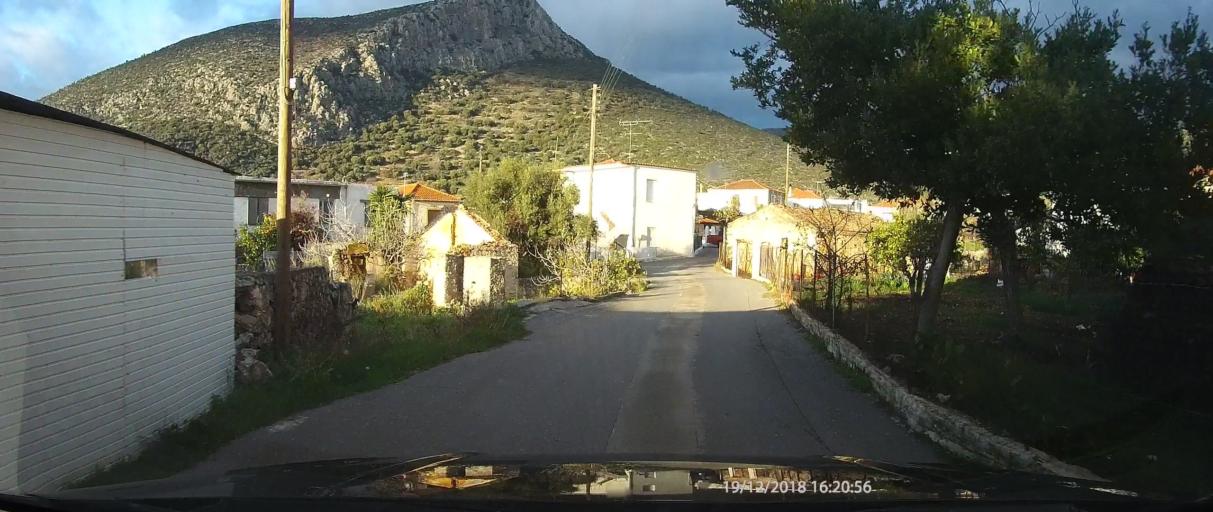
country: GR
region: Peloponnese
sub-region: Nomos Lakonias
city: Kato Glikovrisi
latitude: 36.9360
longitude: 22.8215
